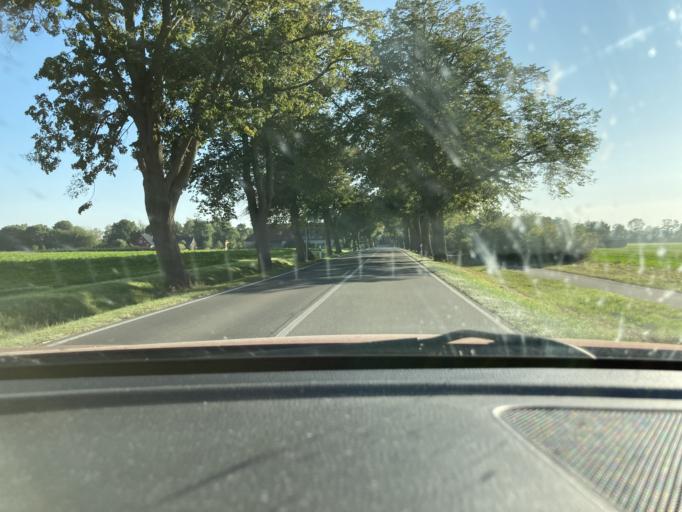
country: DE
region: Mecklenburg-Vorpommern
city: Anklam
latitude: 53.8148
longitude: 13.6792
